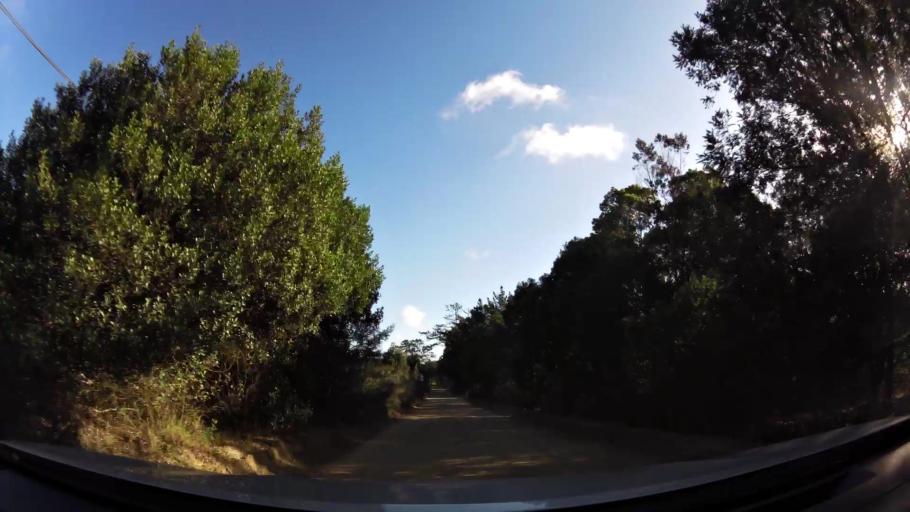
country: ZA
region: Western Cape
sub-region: Eden District Municipality
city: George
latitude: -33.9803
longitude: 22.5713
